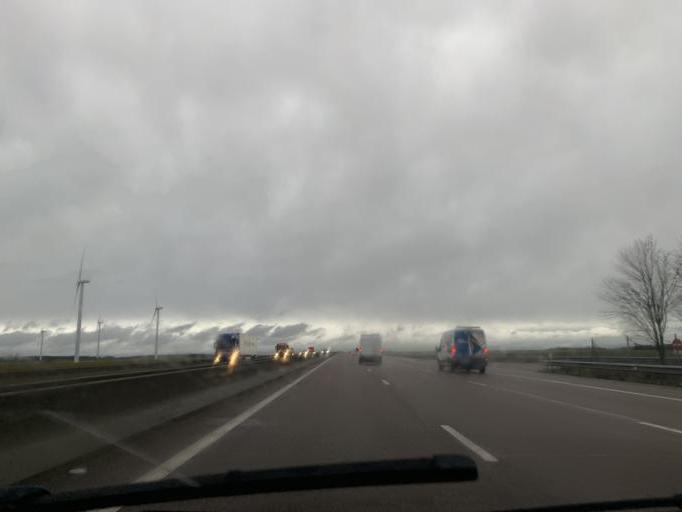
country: FR
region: Bourgogne
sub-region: Departement de la Cote-d'Or
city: Selongey
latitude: 47.7050
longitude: 5.1873
